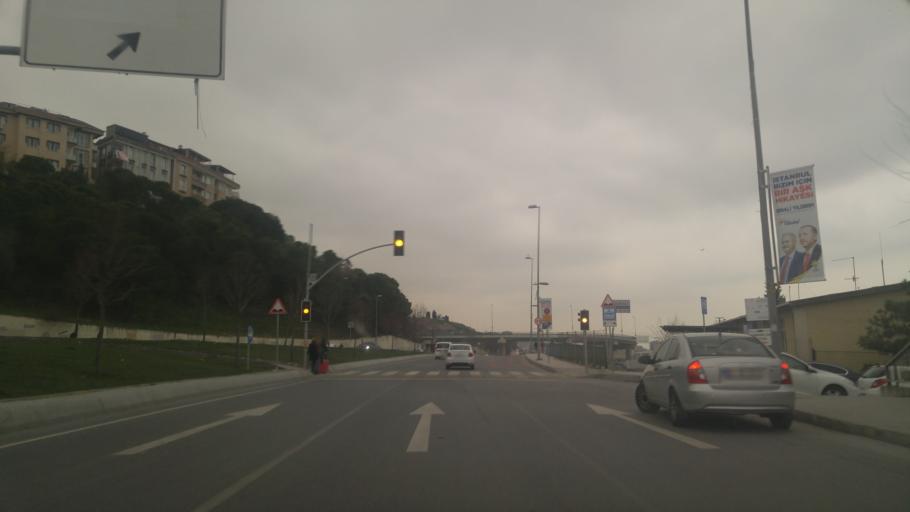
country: TR
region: Istanbul
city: Mahmutbey
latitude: 41.0195
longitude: 28.7681
